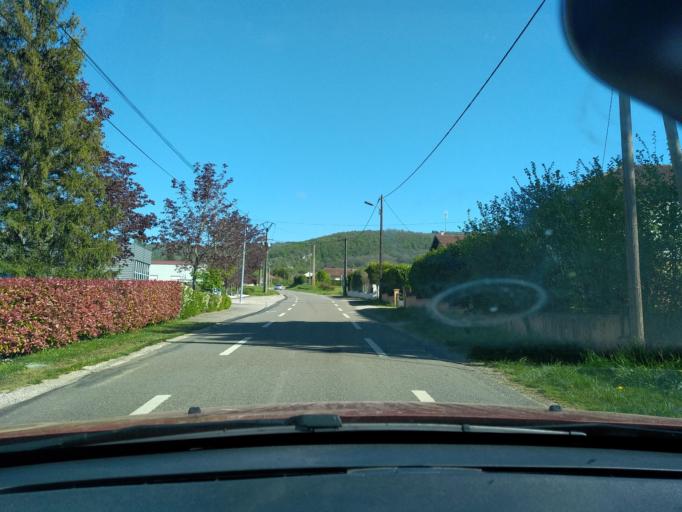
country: FR
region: Franche-Comte
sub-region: Departement du Jura
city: Cousance
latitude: 46.5786
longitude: 5.4335
